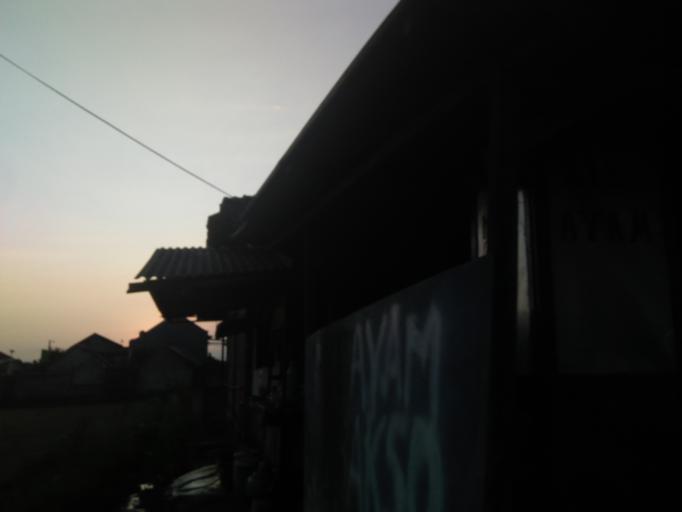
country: ID
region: Daerah Istimewa Yogyakarta
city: Sewon
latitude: -7.8547
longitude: 110.4097
